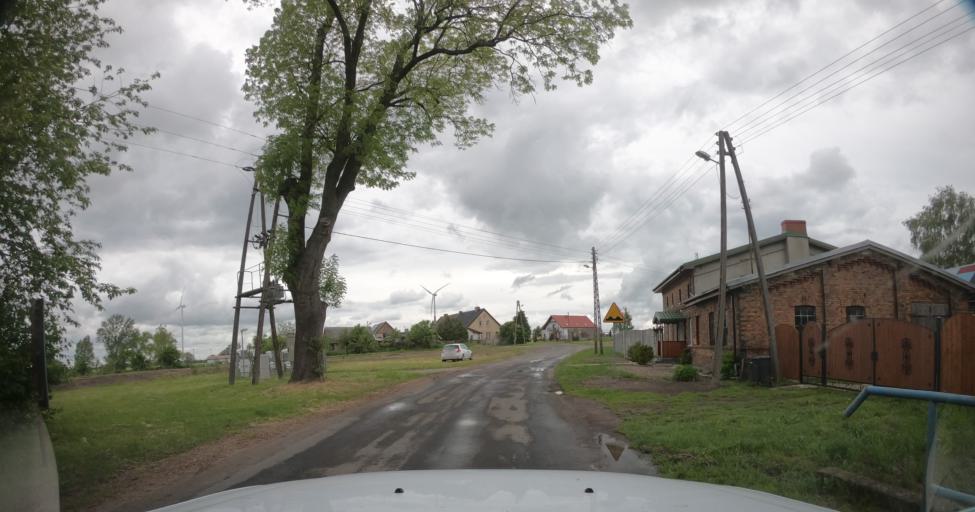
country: PL
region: West Pomeranian Voivodeship
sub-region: Powiat pyrzycki
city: Kozielice
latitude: 53.1090
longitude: 14.8154
